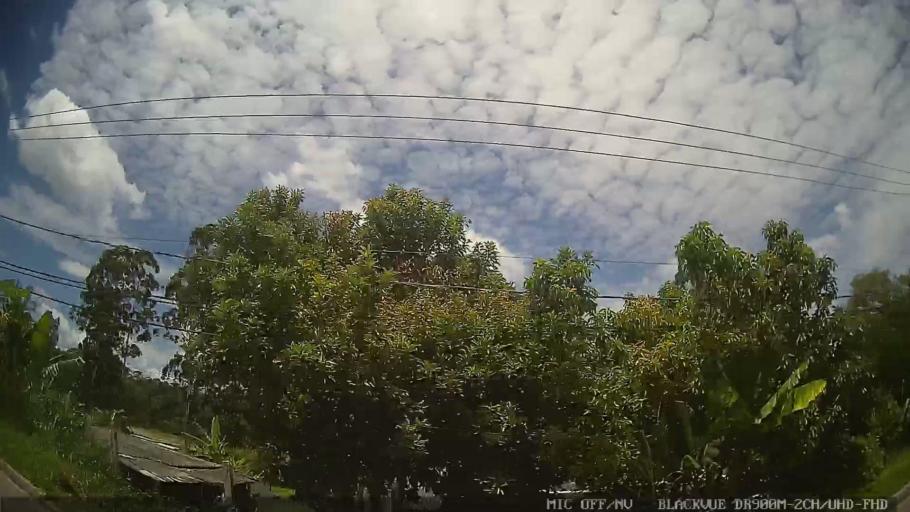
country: BR
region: Sao Paulo
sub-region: Biritiba-Mirim
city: Biritiba Mirim
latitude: -23.5506
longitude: -45.9648
